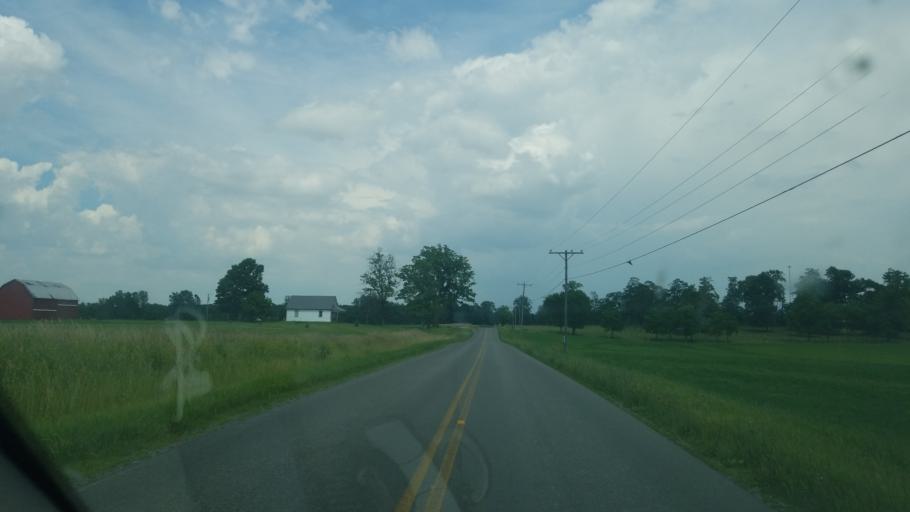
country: US
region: Ohio
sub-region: Logan County
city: Northwood
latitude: 40.4661
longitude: -83.7072
